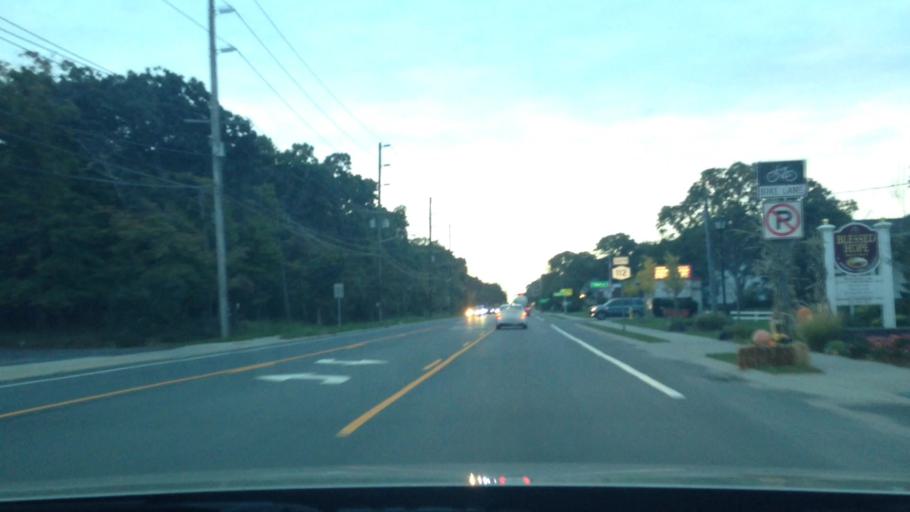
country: US
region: New York
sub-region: Suffolk County
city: Coram
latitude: 40.8635
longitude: -72.9990
